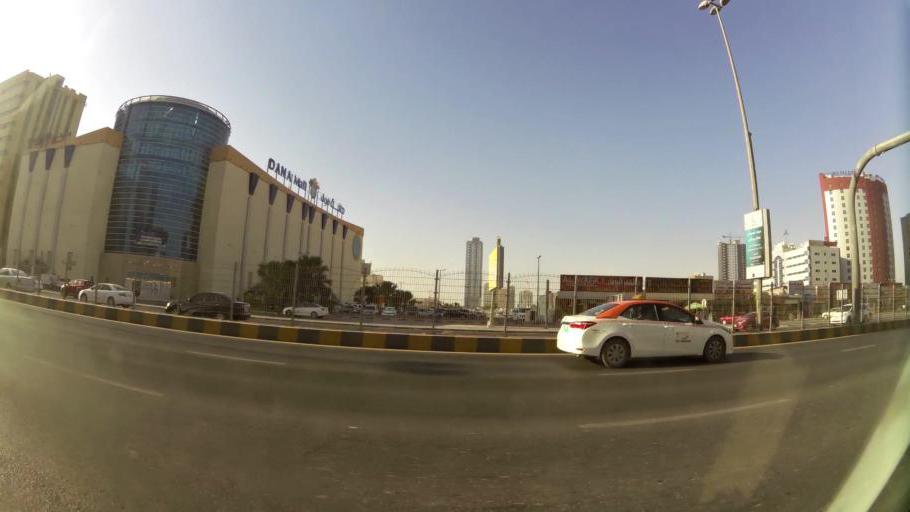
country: AE
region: Ajman
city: Ajman
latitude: 25.3891
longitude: 55.4591
